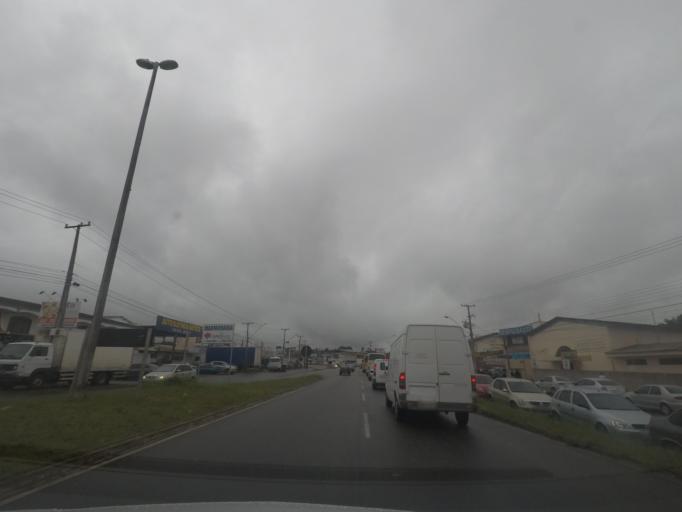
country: BR
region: Parana
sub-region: Colombo
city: Colombo
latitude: -25.3496
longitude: -49.1677
